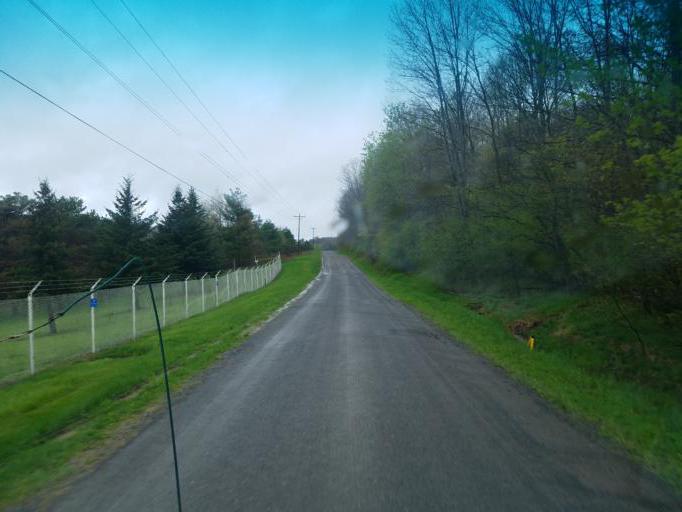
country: US
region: Pennsylvania
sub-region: Tioga County
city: Westfield
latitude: 41.9805
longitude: -77.6883
